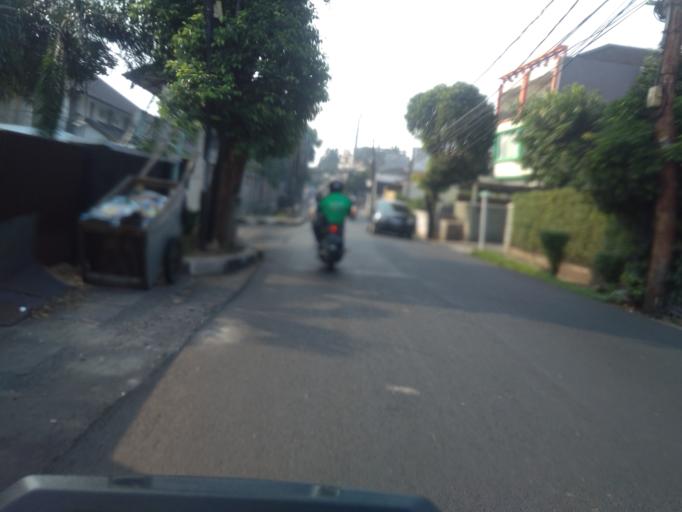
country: ID
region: Jakarta Raya
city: Jakarta
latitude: -6.2644
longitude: 106.8326
